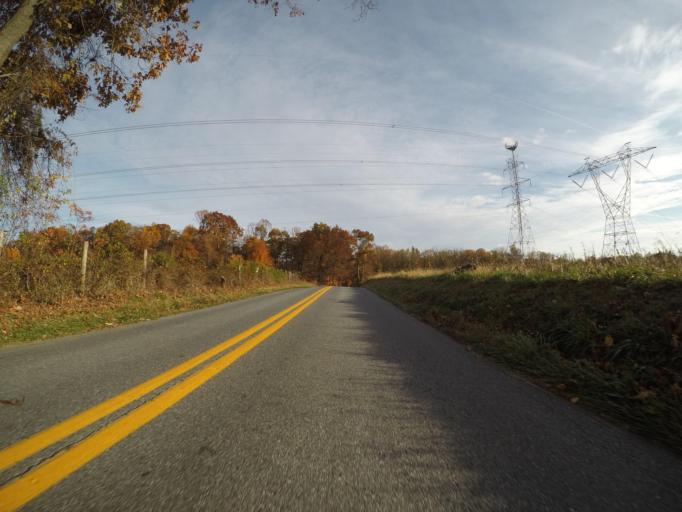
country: US
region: Maryland
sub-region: Baltimore County
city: Reisterstown
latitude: 39.5298
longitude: -76.7805
